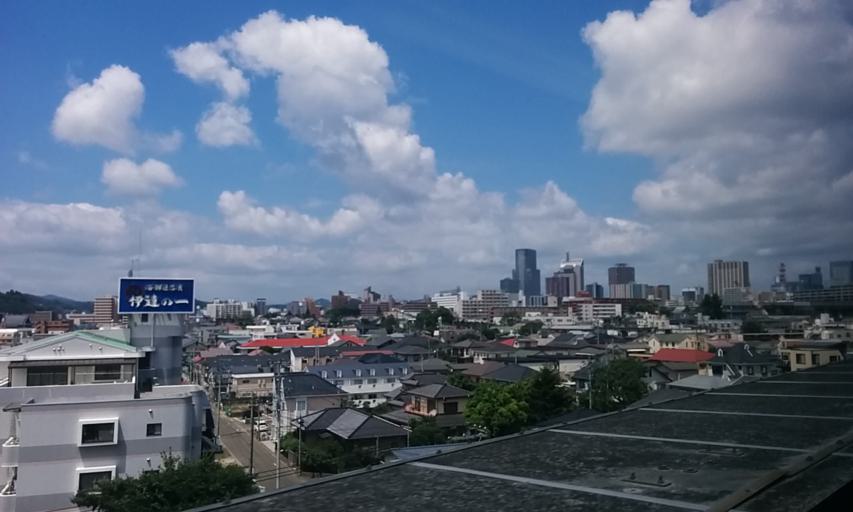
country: JP
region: Miyagi
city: Sendai
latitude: 38.2446
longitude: 140.8929
